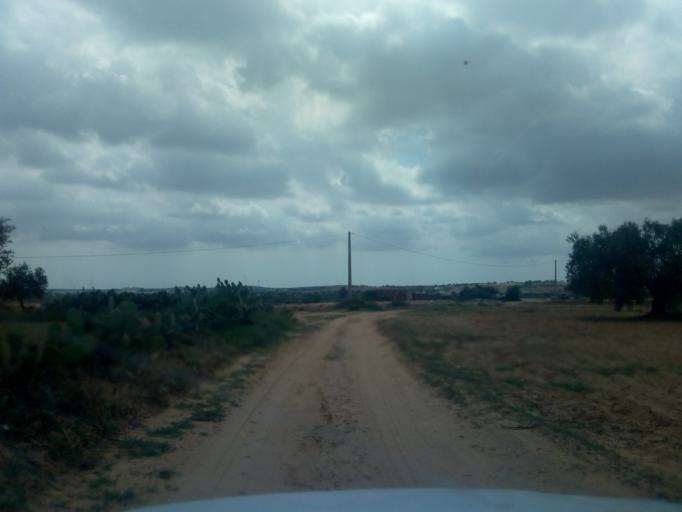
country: TN
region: Safaqis
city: Sfax
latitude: 34.7428
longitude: 10.4927
